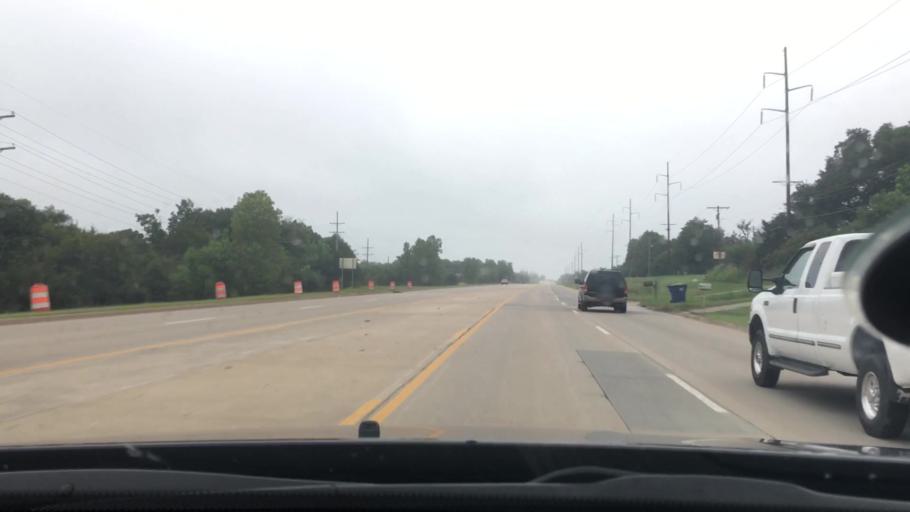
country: US
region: Oklahoma
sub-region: Seminole County
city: Seminole
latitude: 35.2503
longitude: -96.6711
